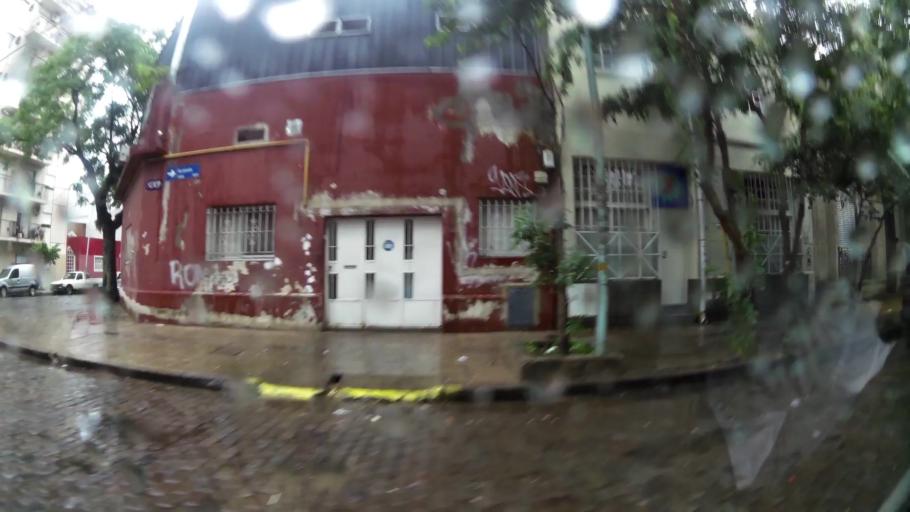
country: AR
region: Buenos Aires F.D.
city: Colegiales
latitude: -34.5937
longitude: -58.4339
